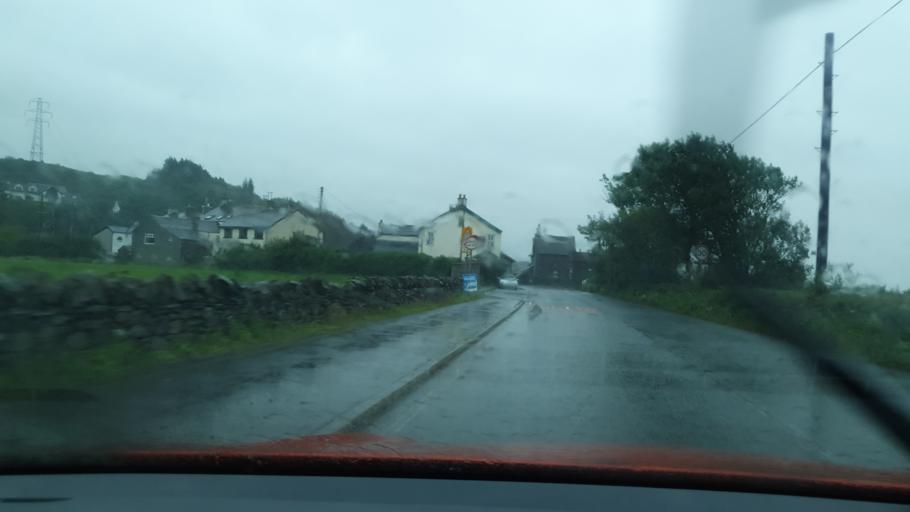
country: GB
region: England
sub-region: Cumbria
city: Millom
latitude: 54.2597
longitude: -3.2163
